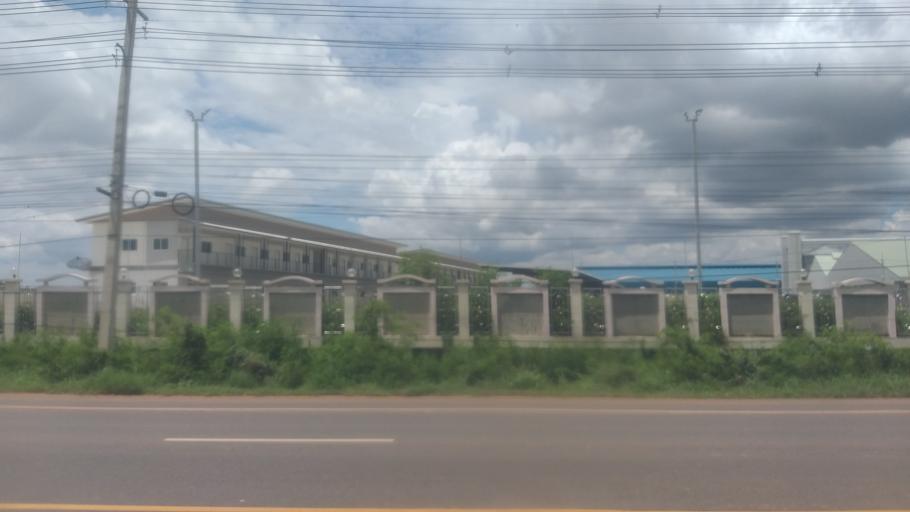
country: TH
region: Nakhon Ratchasima
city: Non Thai
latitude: 15.0896
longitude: 102.1103
